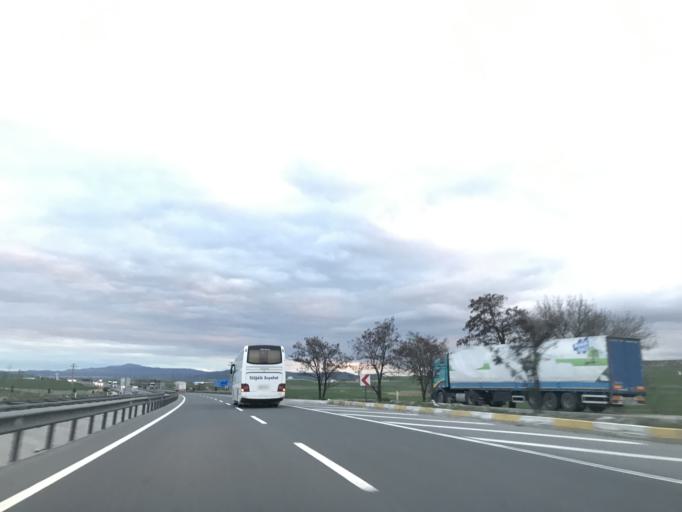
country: TR
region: Ankara
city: Ikizce
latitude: 39.4605
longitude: 32.8627
